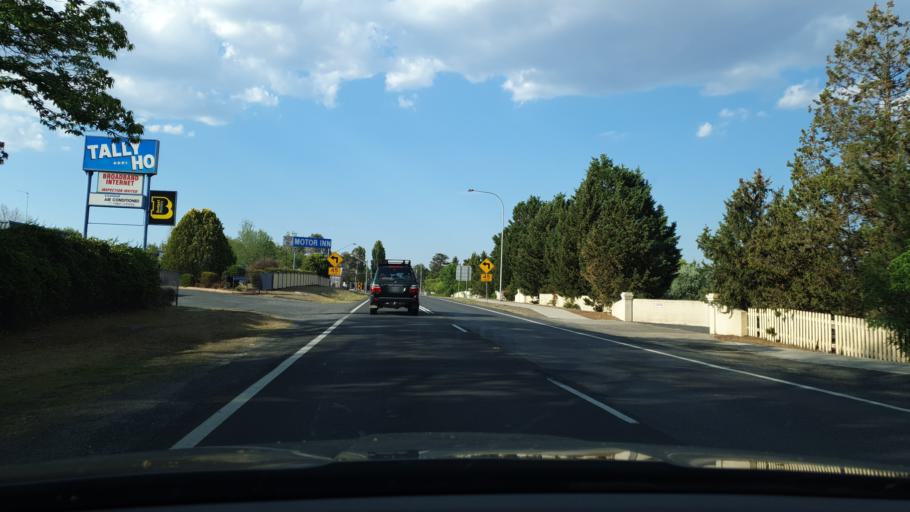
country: AU
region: New South Wales
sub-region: Tenterfield Municipality
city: Carrolls Creek
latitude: -29.0428
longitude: 152.0211
